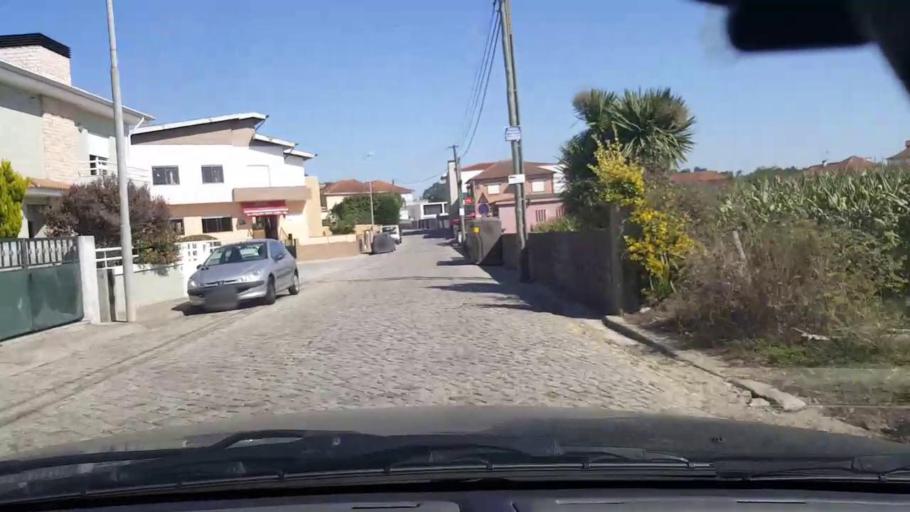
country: PT
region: Porto
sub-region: Matosinhos
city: Lavra
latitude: 41.2947
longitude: -8.6935
